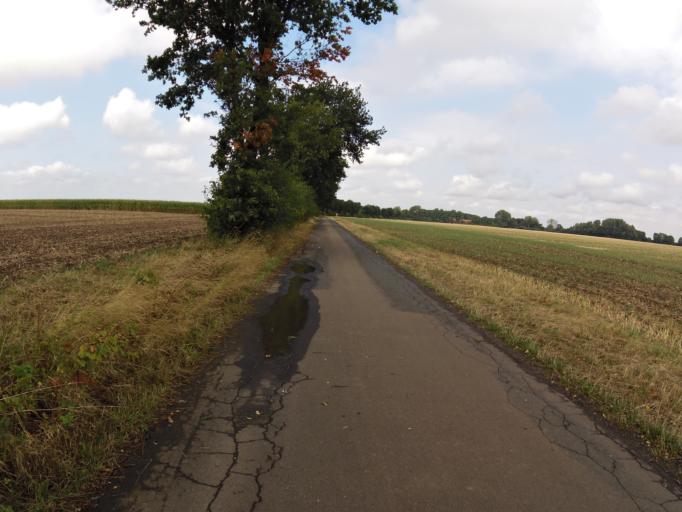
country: DE
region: Lower Saxony
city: Schweringen
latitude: 52.7637
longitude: 9.1774
